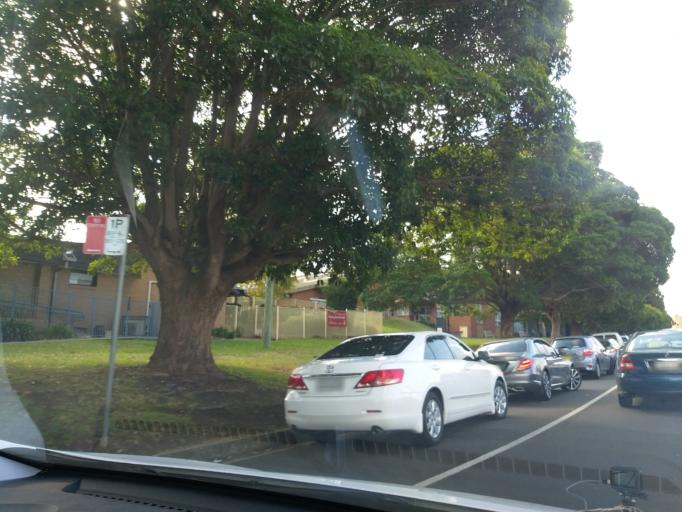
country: AU
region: New South Wales
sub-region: Wollongong
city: Helensburgh
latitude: -34.1930
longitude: 150.9816
